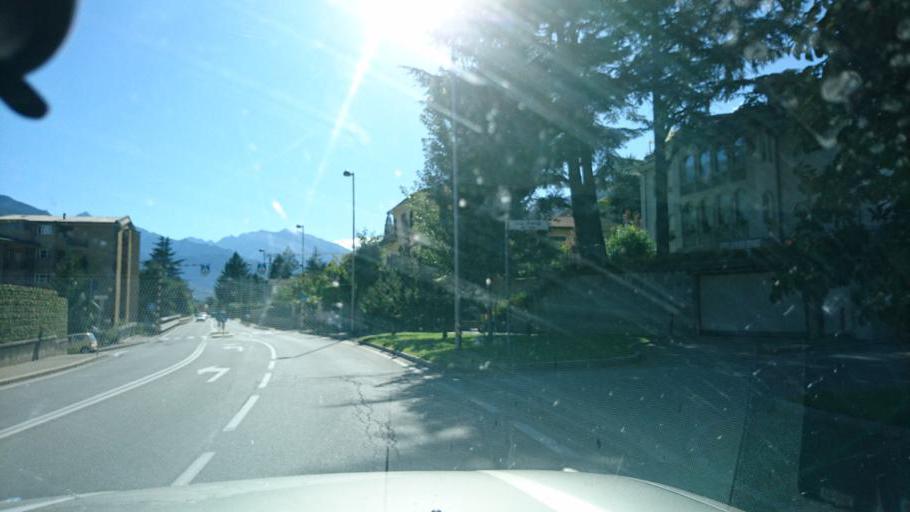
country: IT
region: Aosta Valley
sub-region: Valle d'Aosta
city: Aosta
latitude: 45.7415
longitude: 7.3128
